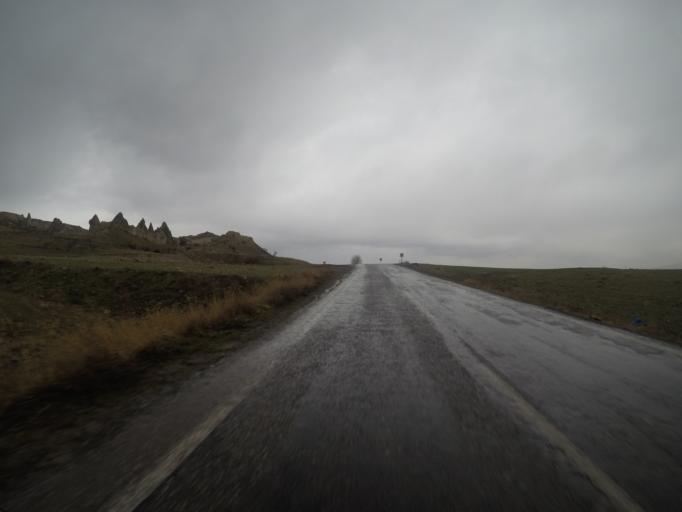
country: TR
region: Nevsehir
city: Goereme
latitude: 38.6658
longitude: 34.8270
